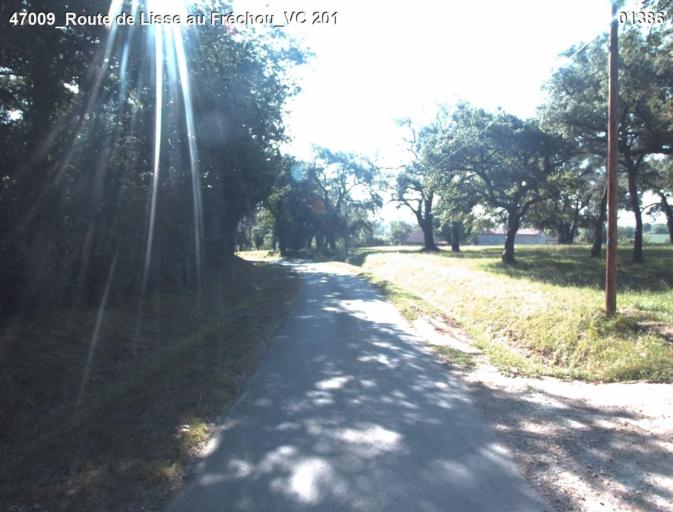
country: FR
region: Aquitaine
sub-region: Departement du Lot-et-Garonne
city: Mezin
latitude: 44.0921
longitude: 0.2948
